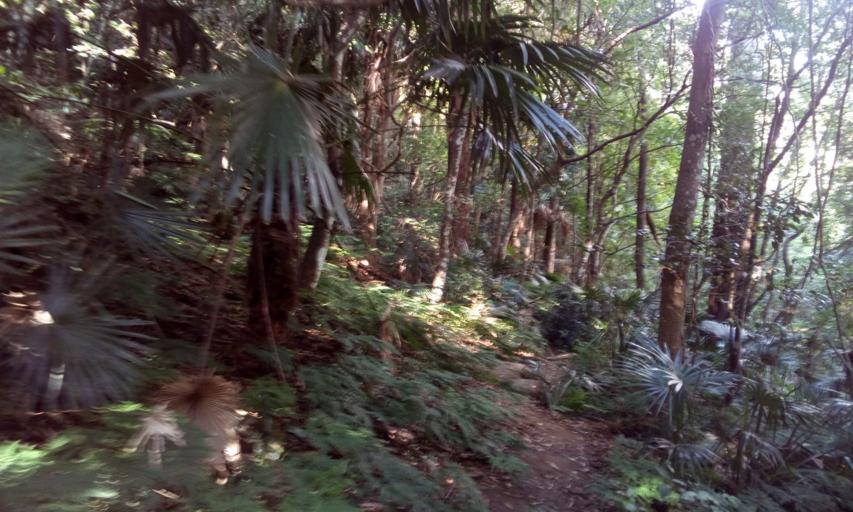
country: AU
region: New South Wales
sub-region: Wollongong
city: Cordeaux Heights
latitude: -34.4414
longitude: 150.7929
